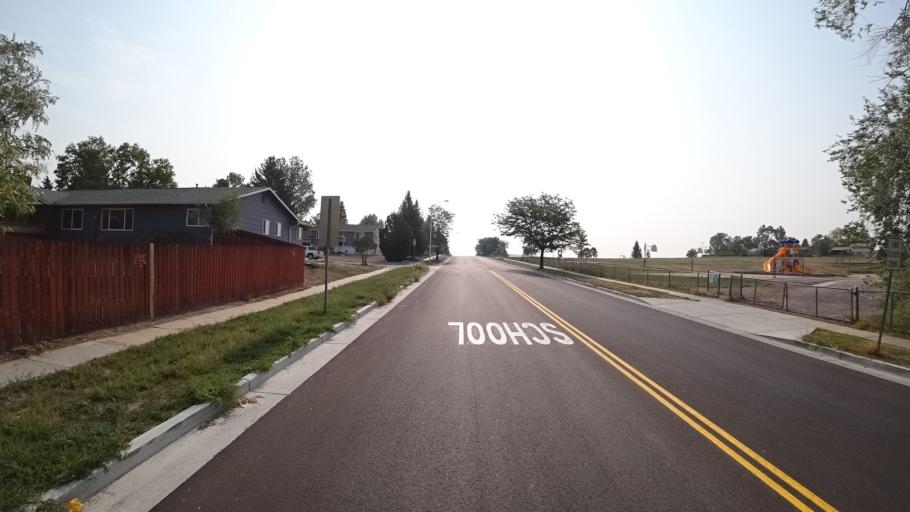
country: US
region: Colorado
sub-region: El Paso County
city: Stratmoor
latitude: 38.8114
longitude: -104.7700
